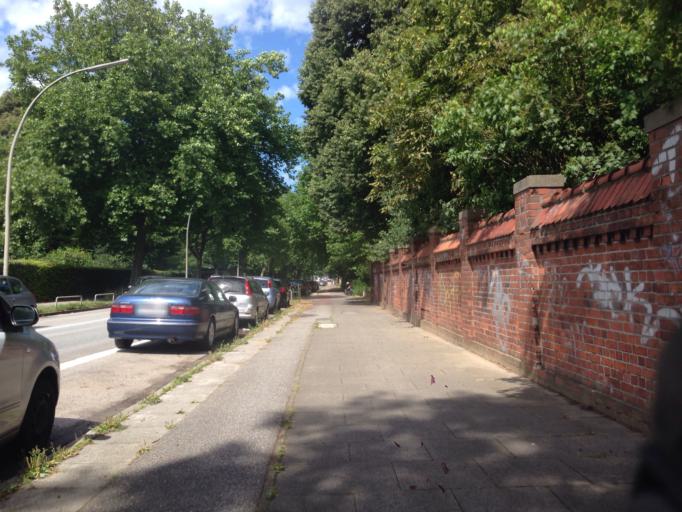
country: DE
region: Hamburg
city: Barmbek-Nord
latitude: 53.6025
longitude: 10.0354
